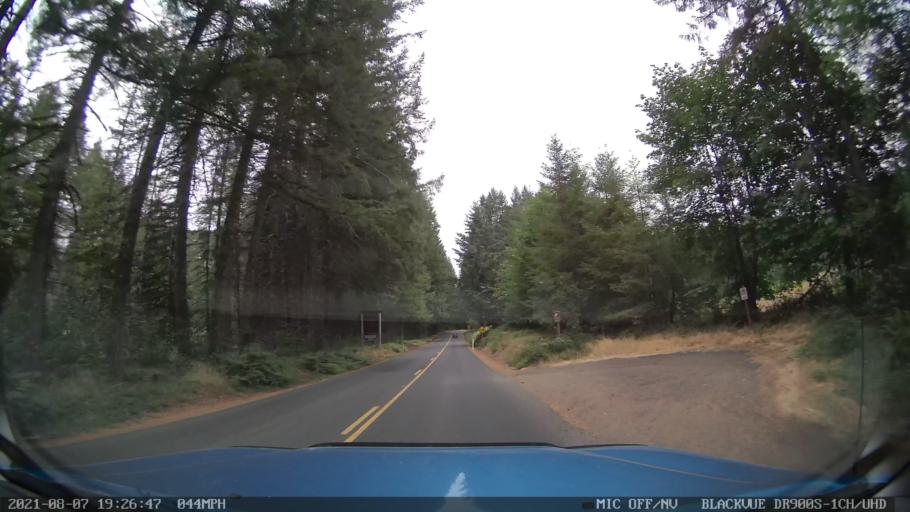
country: US
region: Oregon
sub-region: Linn County
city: Lyons
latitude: 44.8755
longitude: -122.6515
